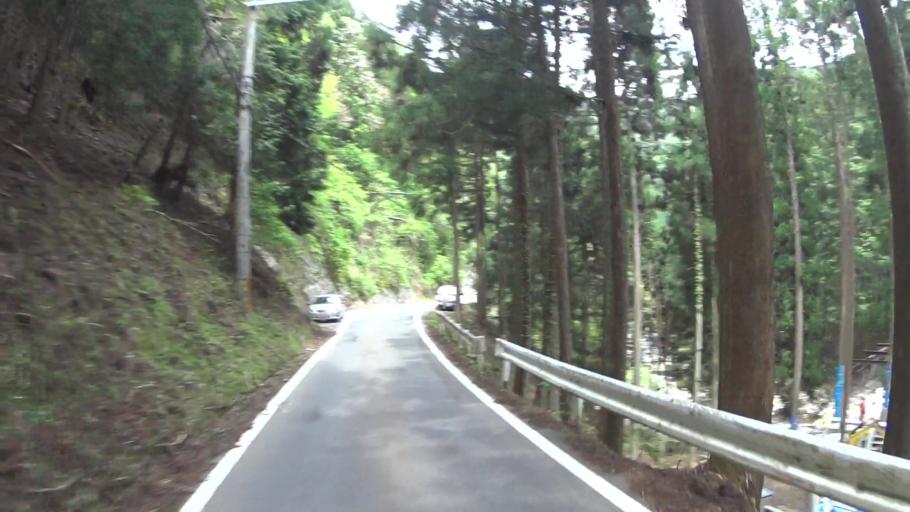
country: JP
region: Kyoto
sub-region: Kyoto-shi
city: Kamigyo-ku
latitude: 35.1975
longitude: 135.7477
